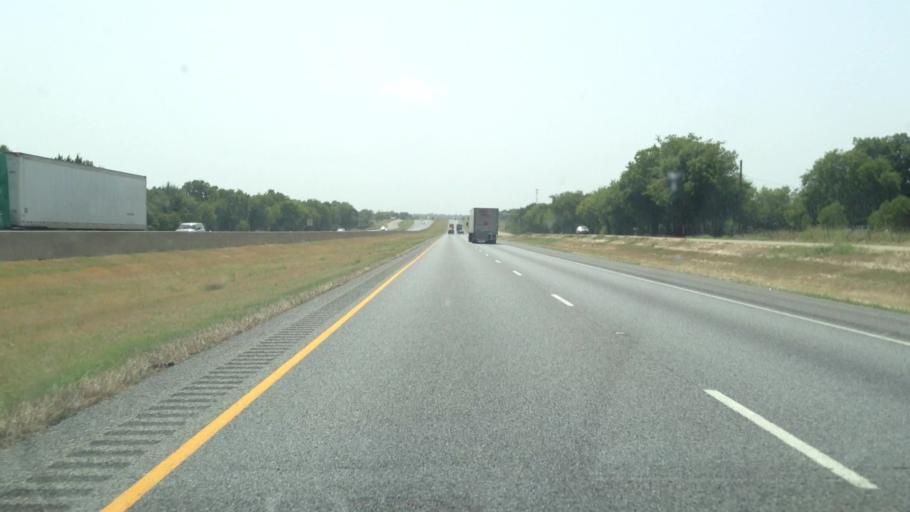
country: US
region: Texas
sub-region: Hunt County
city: Commerce
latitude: 33.1317
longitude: -95.9267
